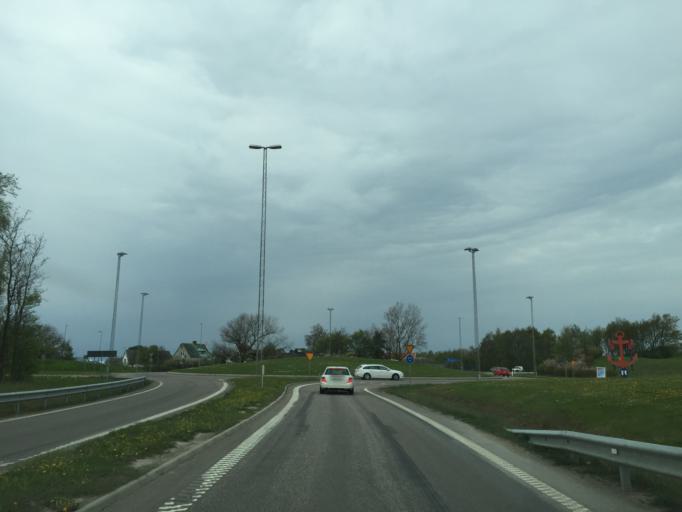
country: SE
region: Skane
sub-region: Hoganas Kommun
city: Hoganas
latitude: 56.1715
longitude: 12.5652
